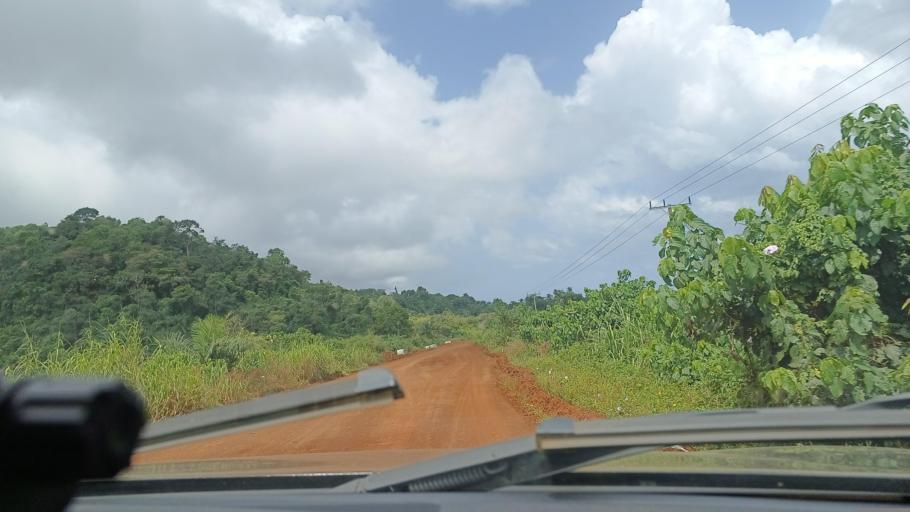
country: LR
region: Grand Cape Mount
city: Robertsport
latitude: 6.7492
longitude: -11.3592
